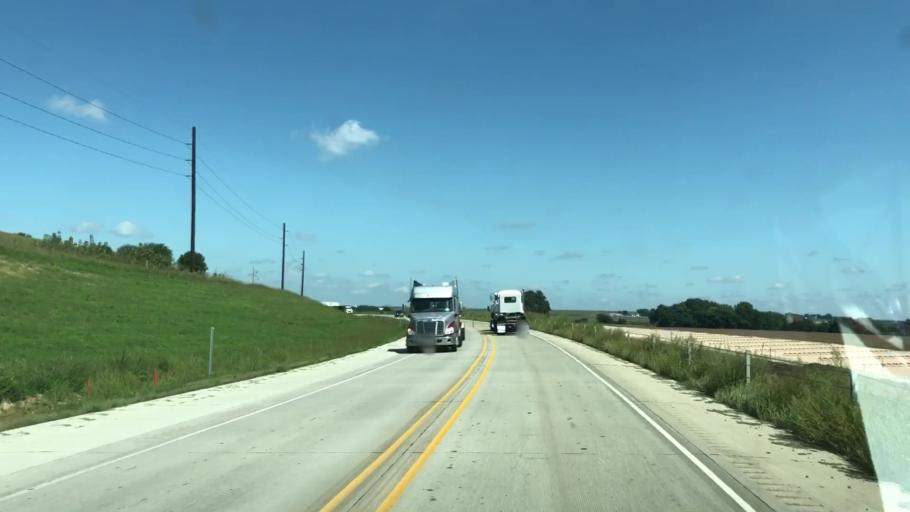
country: US
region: Iowa
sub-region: Plymouth County
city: Le Mars
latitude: 42.7379
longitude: -96.2183
